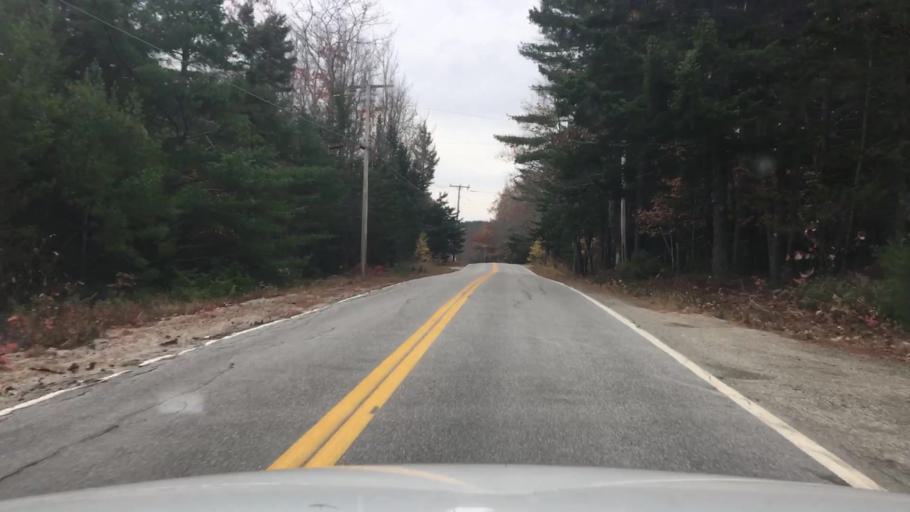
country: US
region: Maine
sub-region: Hancock County
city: Sedgwick
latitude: 44.3335
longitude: -68.5669
